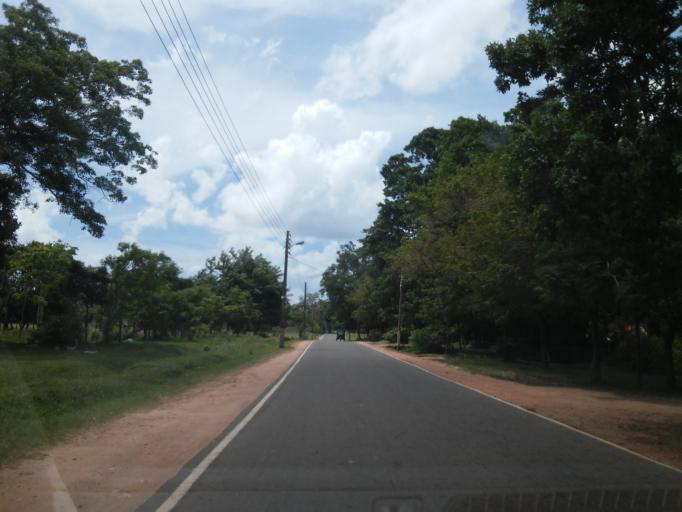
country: LK
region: North Central
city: Anuradhapura
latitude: 8.3526
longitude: 80.3983
